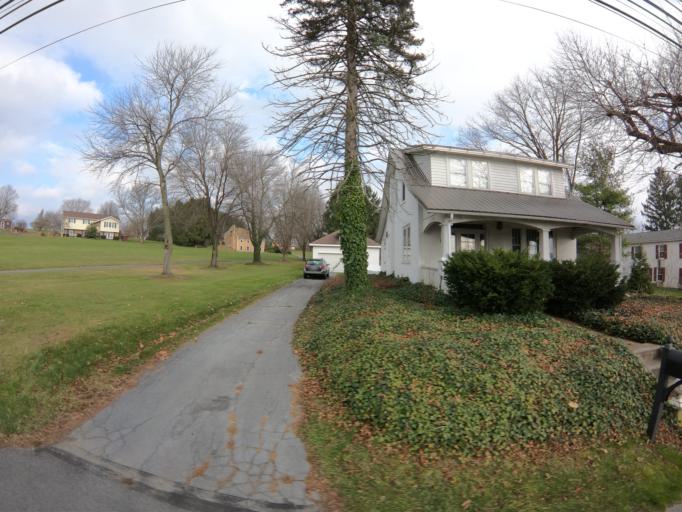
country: US
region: Pennsylvania
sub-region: Lancaster County
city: Maytown
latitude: 40.0715
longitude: -76.5786
